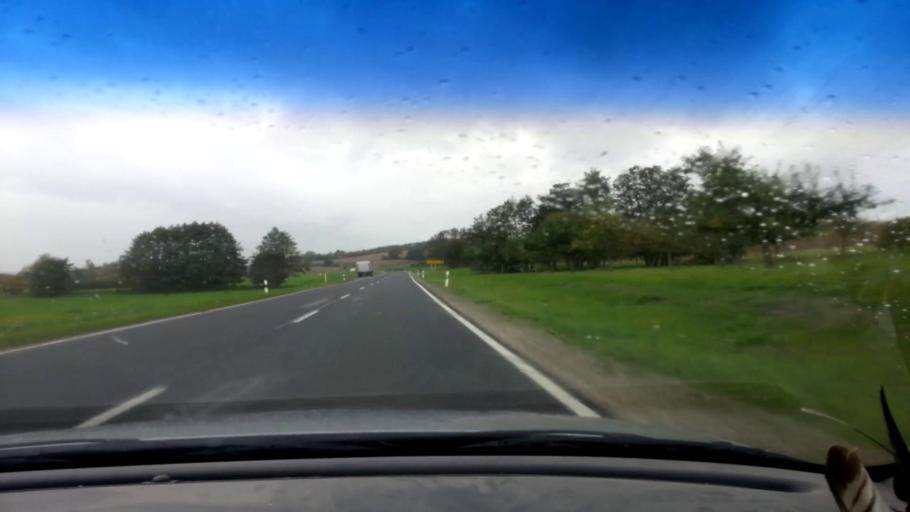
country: DE
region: Bavaria
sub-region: Upper Franconia
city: Stegaurach
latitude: 49.8676
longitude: 10.8305
